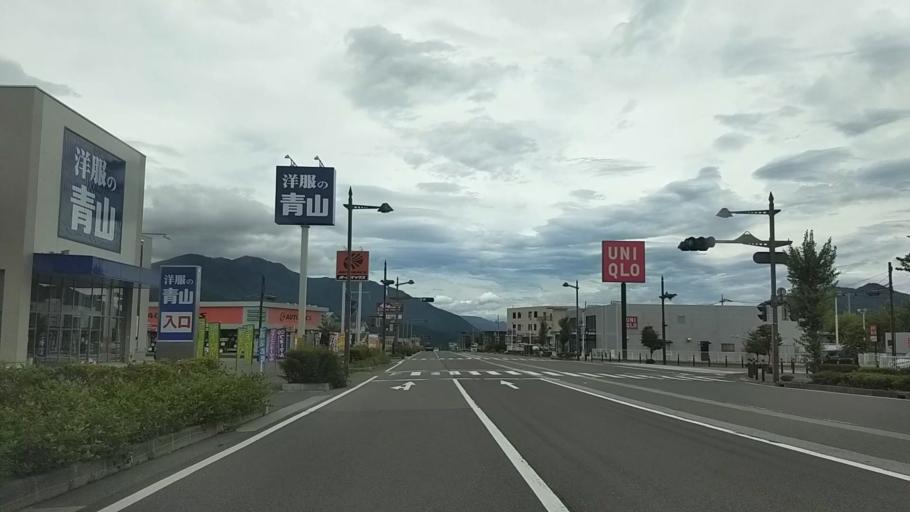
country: JP
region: Yamanashi
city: Fujikawaguchiko
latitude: 35.4688
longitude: 138.8056
